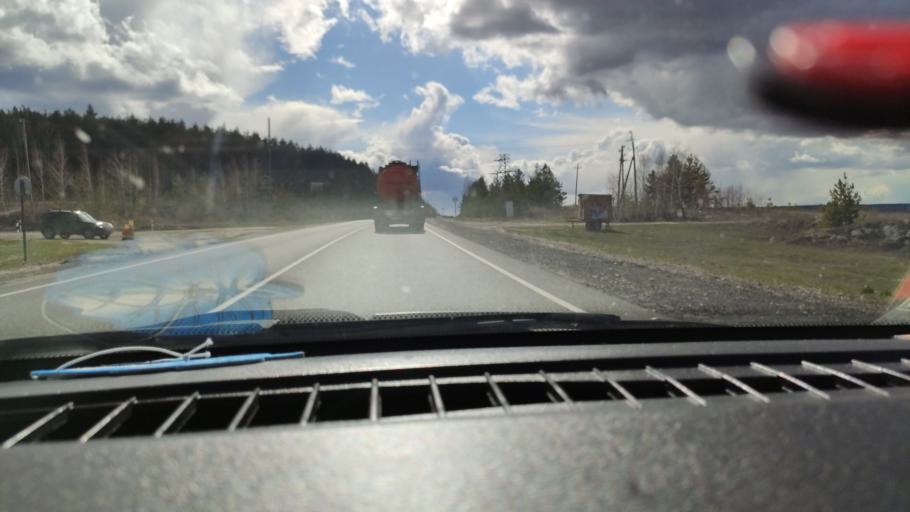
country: RU
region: Saratov
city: Khvalynsk
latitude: 52.5413
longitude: 48.0569
